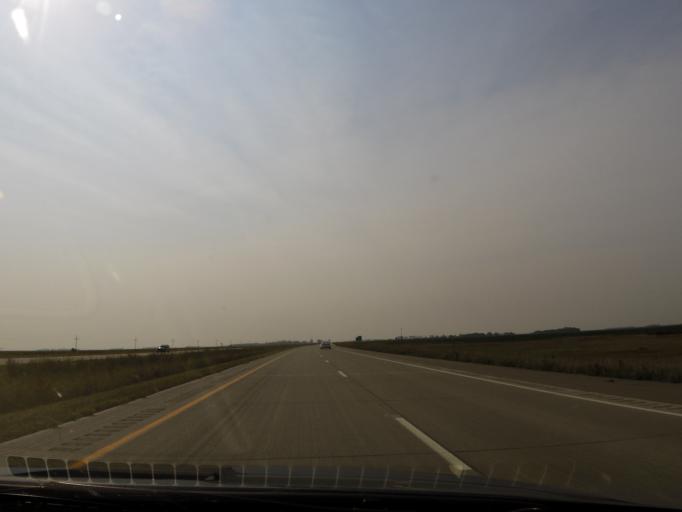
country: US
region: North Dakota
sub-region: Traill County
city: Hillsboro
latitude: 47.1744
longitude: -96.9804
